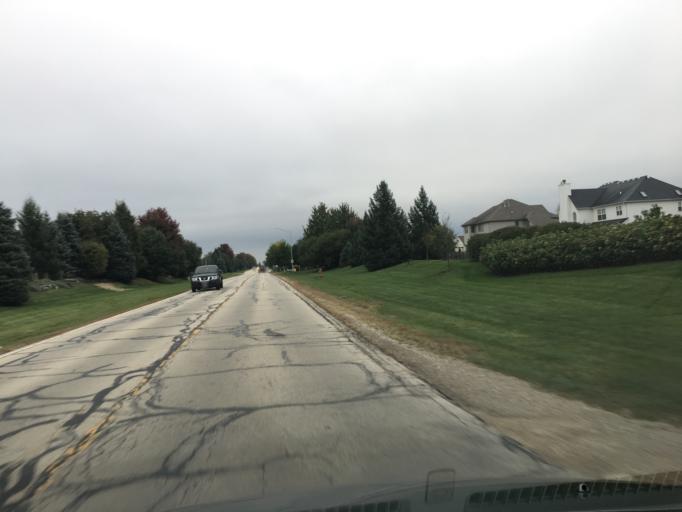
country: US
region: Illinois
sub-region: Will County
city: Plainfield
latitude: 41.6521
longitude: -88.1766
